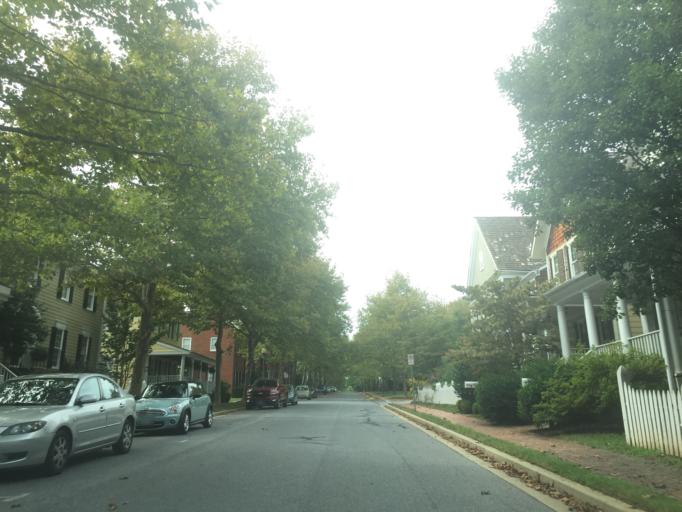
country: US
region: Maryland
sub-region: Montgomery County
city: North Potomac
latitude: 39.1146
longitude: -77.2428
